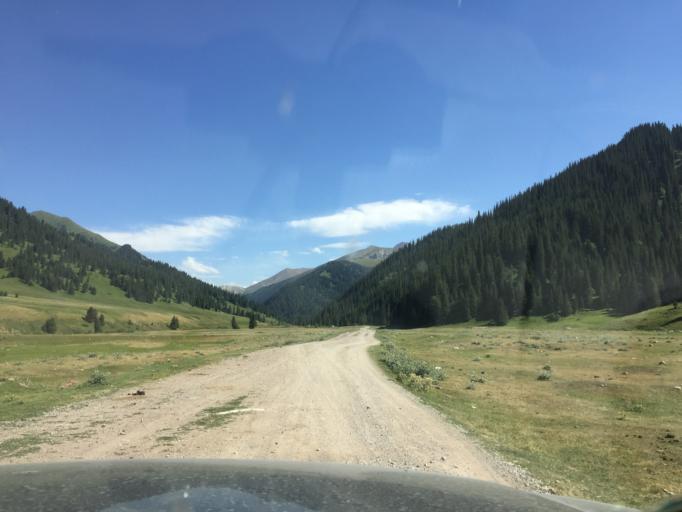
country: KZ
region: Almaty Oblysy
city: Kegen
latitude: 42.6735
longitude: 79.2003
